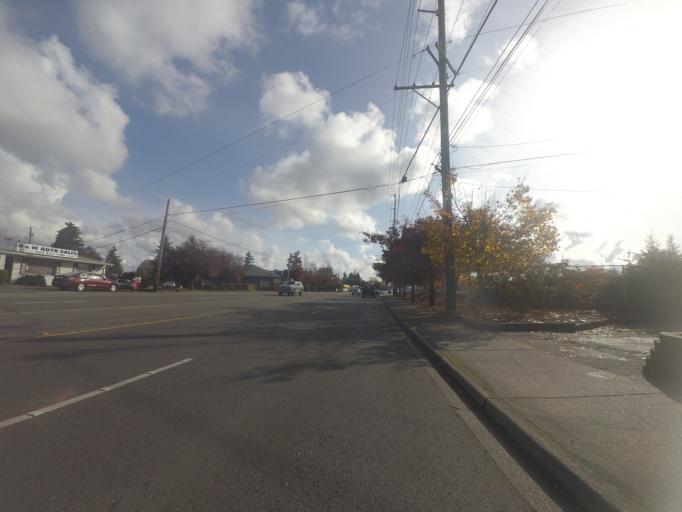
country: US
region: Washington
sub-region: Pierce County
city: Lakewood
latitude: 47.1633
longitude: -122.5064
